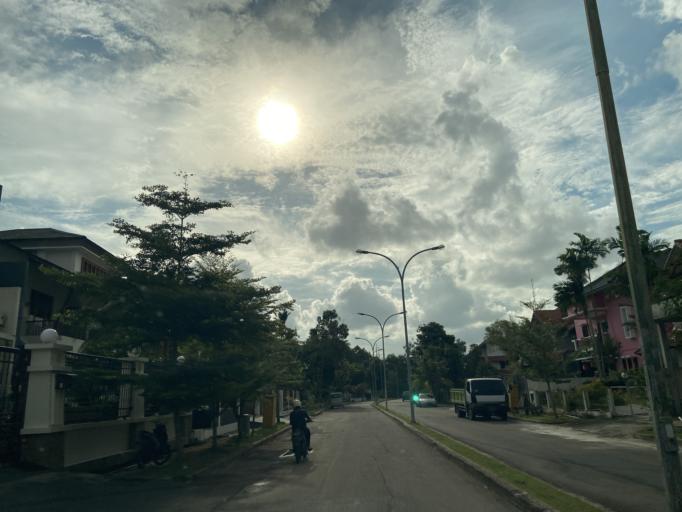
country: SG
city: Singapore
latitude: 1.1090
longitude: 104.0255
